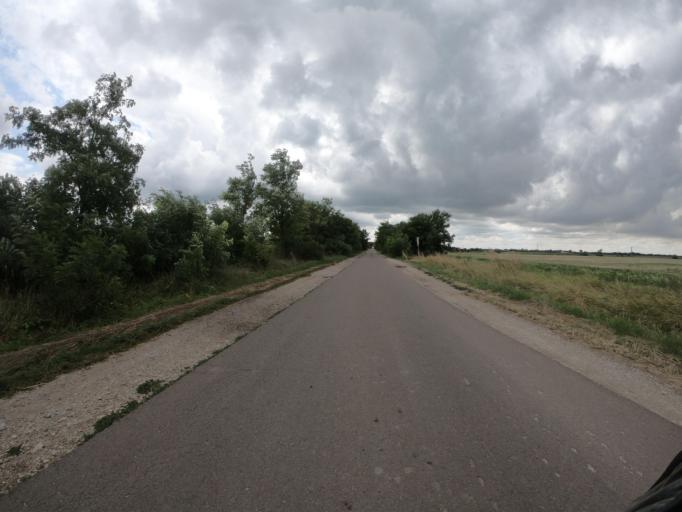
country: HU
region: Heves
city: Poroszlo
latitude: 47.7066
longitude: 20.7009
